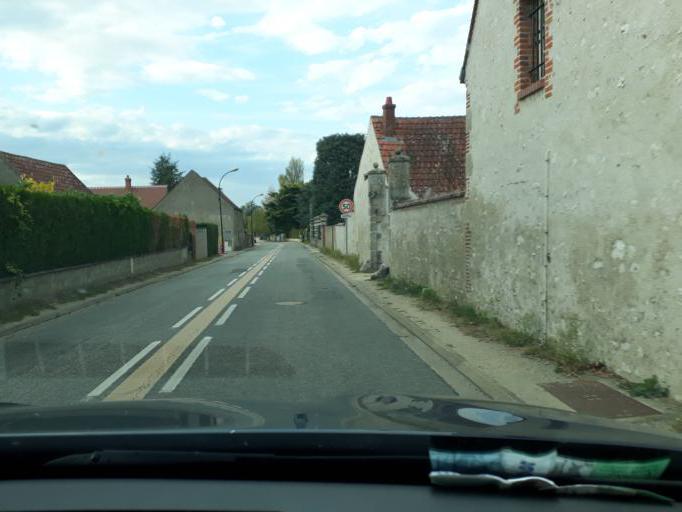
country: FR
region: Centre
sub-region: Departement du Loiret
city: Saint-Benoit-sur-Loire
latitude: 47.8129
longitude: 2.3029
